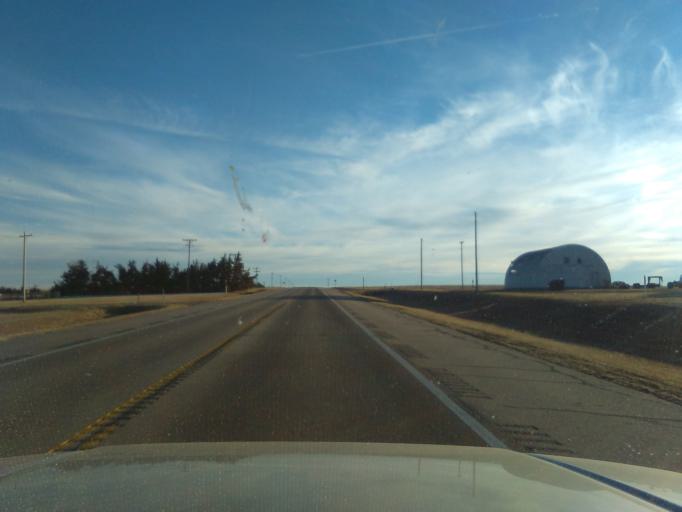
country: US
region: Kansas
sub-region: Logan County
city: Oakley
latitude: 39.1781
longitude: -100.8704
